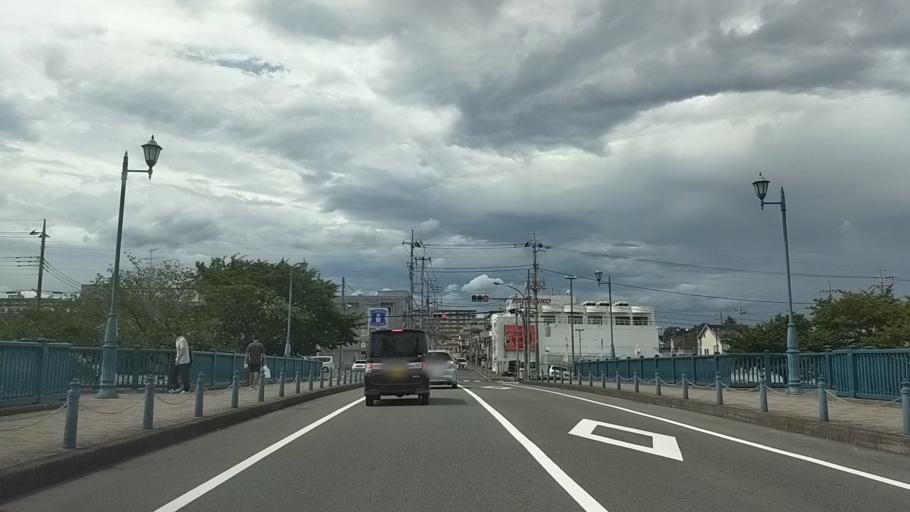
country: JP
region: Tokyo
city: Hachioji
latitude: 35.6531
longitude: 139.3004
